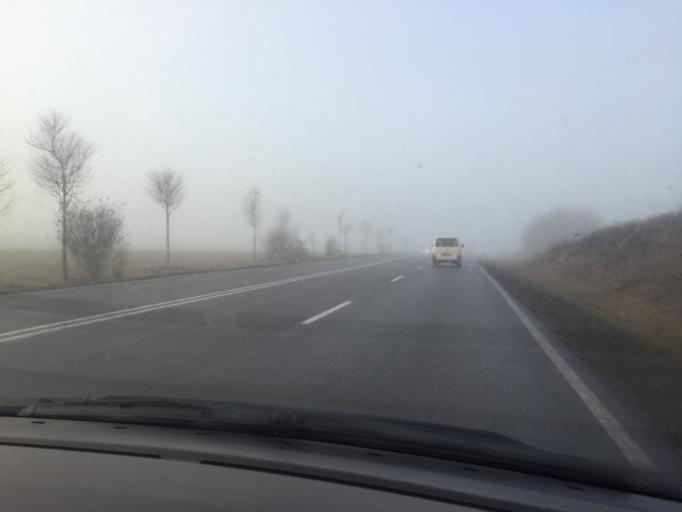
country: DE
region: Baden-Wuerttemberg
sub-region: Freiburg Region
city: Braunlingen
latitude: 47.9007
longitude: 8.4544
